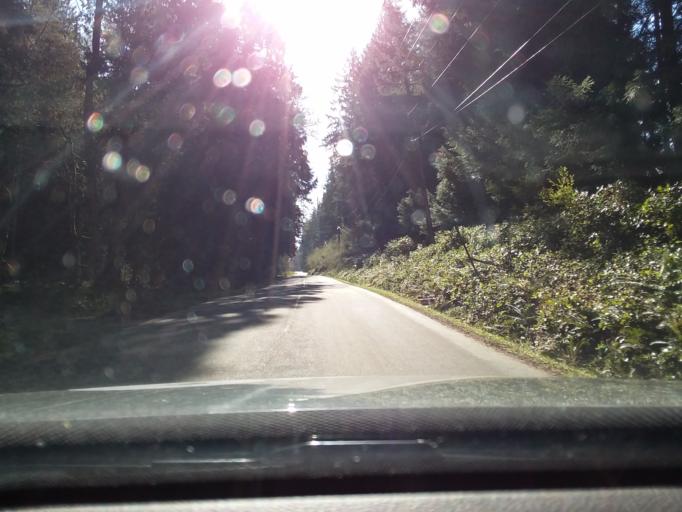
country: CA
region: British Columbia
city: North Cowichan
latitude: 48.9338
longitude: -123.4759
